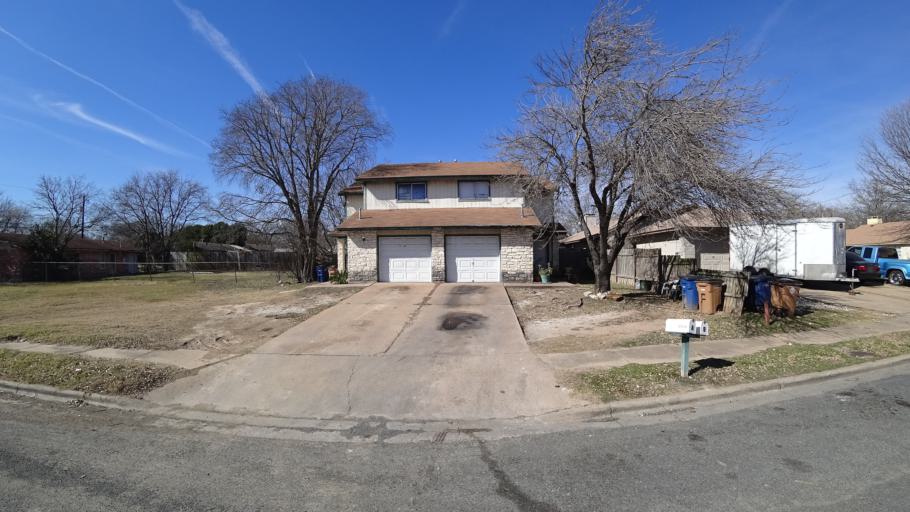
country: US
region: Texas
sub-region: Travis County
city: Wells Branch
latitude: 30.3775
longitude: -97.6933
